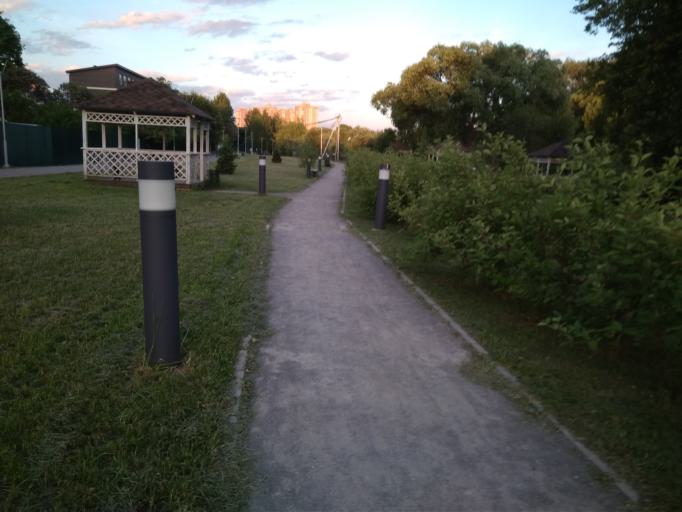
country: RU
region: Moskovskaya
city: Troitsk
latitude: 55.4962
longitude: 37.3013
